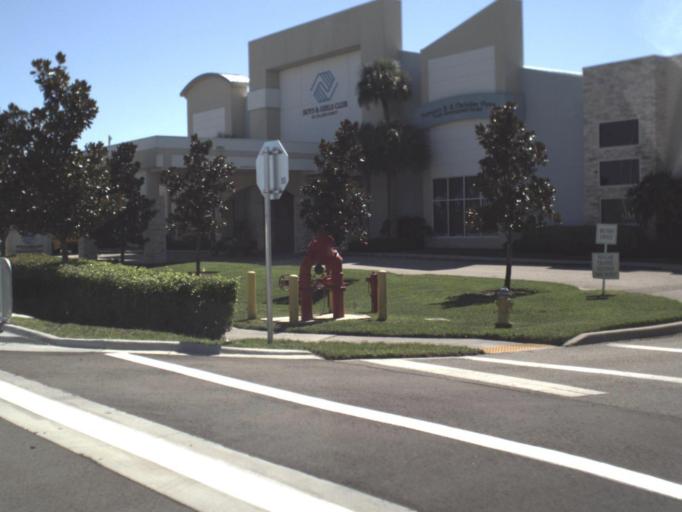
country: US
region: Florida
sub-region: Collier County
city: Lely
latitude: 26.1388
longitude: -81.7163
